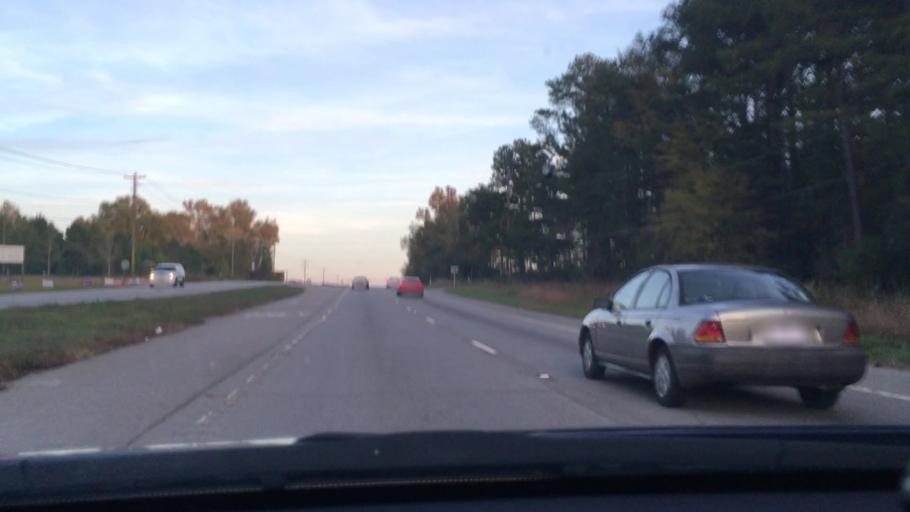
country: US
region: South Carolina
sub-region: Richland County
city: Hopkins
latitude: 33.9445
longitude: -80.8879
